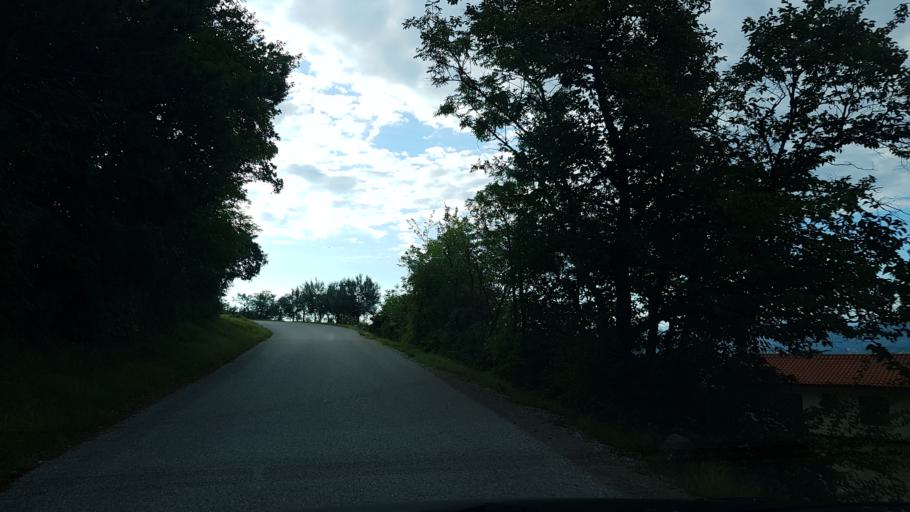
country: SI
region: Rence-Vogrsko
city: Rence
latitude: 45.8713
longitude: 13.6571
